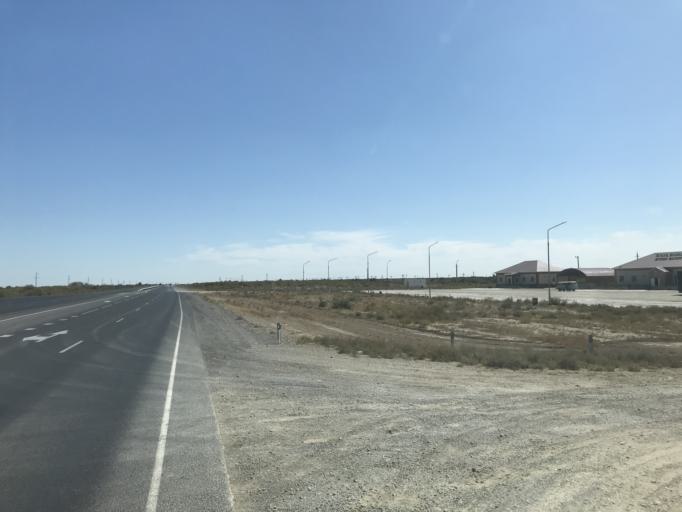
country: KZ
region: Qyzylorda
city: Belkol
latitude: 44.7656
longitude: 65.7788
